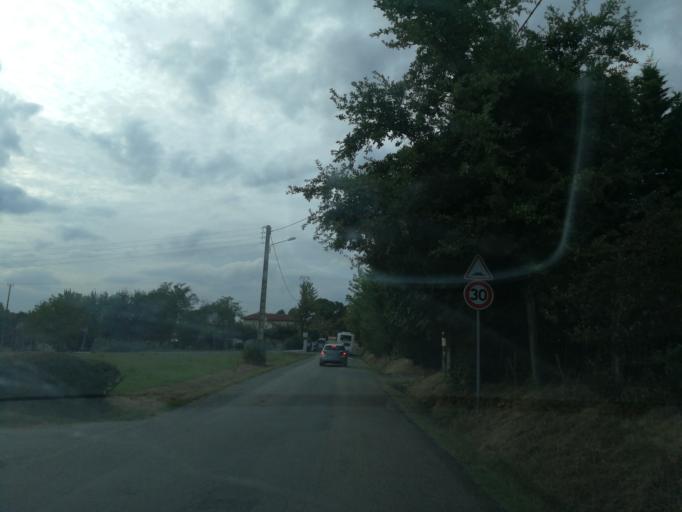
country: FR
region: Midi-Pyrenees
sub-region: Departement de la Haute-Garonne
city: Flourens
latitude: 43.5895
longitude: 1.5799
